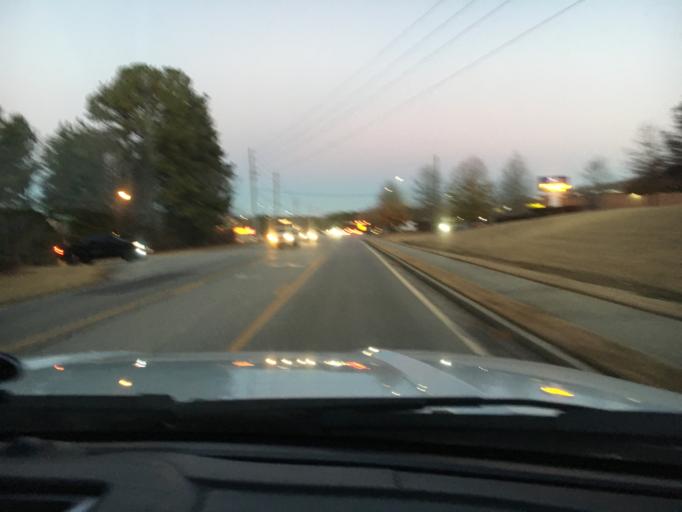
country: US
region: Georgia
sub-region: Jackson County
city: Jefferson
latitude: 34.1227
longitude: -83.6091
